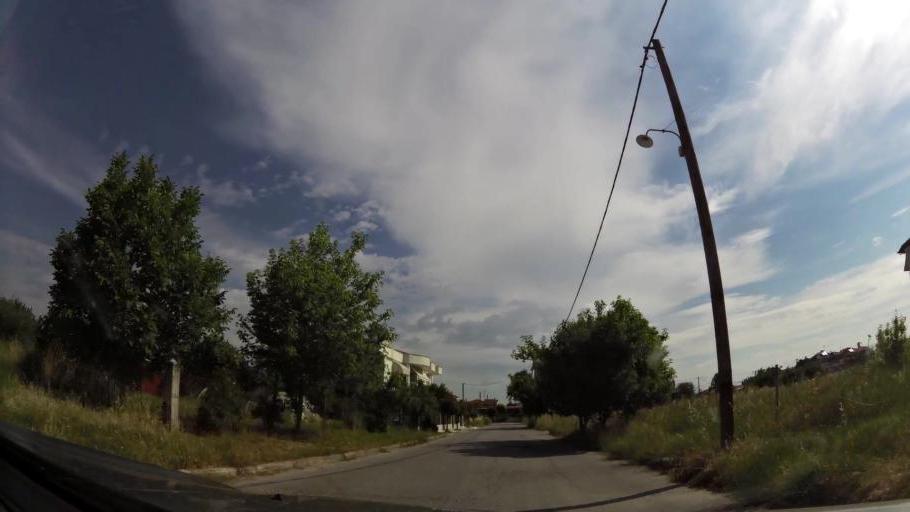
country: GR
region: Central Macedonia
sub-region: Nomos Pierias
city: Katerini
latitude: 40.2819
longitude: 22.4962
